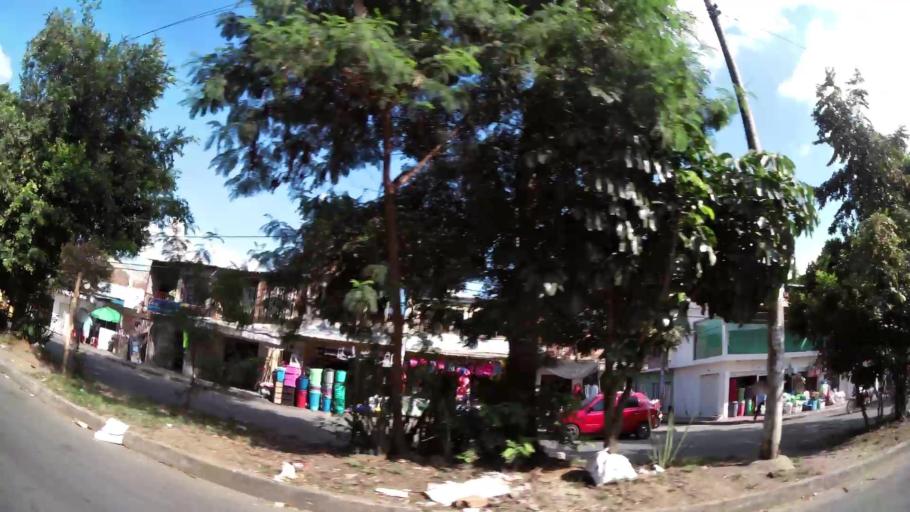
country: CO
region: Valle del Cauca
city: Cali
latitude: 3.4201
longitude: -76.4931
